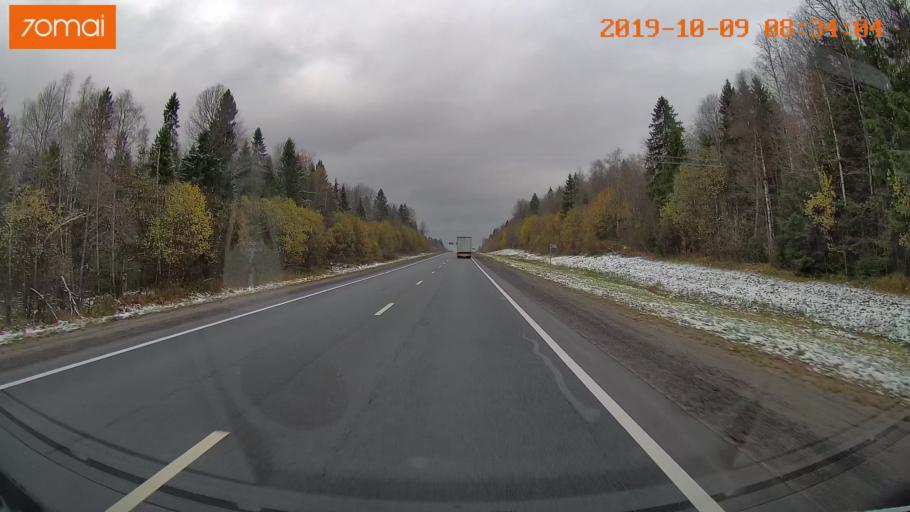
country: RU
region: Vologda
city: Gryazovets
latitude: 58.8916
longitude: 40.1880
